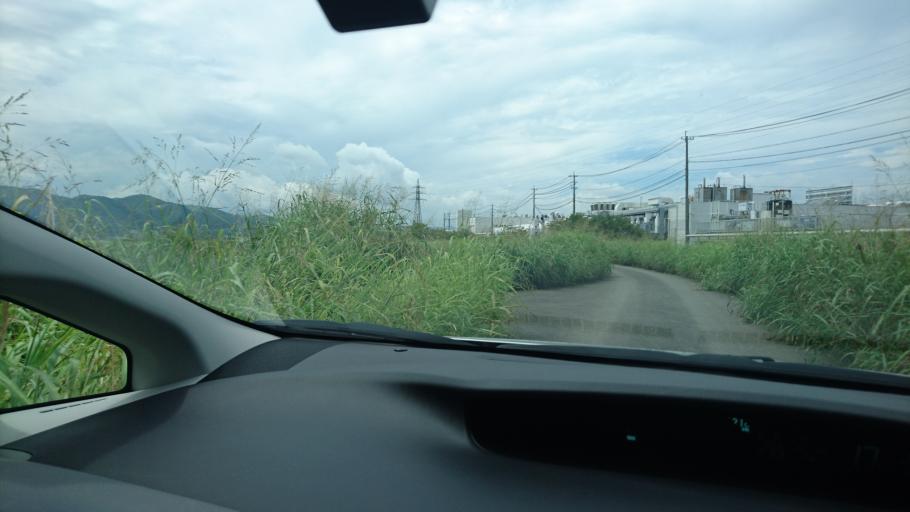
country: JP
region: Saga Prefecture
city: Takeocho-takeo
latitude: 33.2109
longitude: 130.1109
